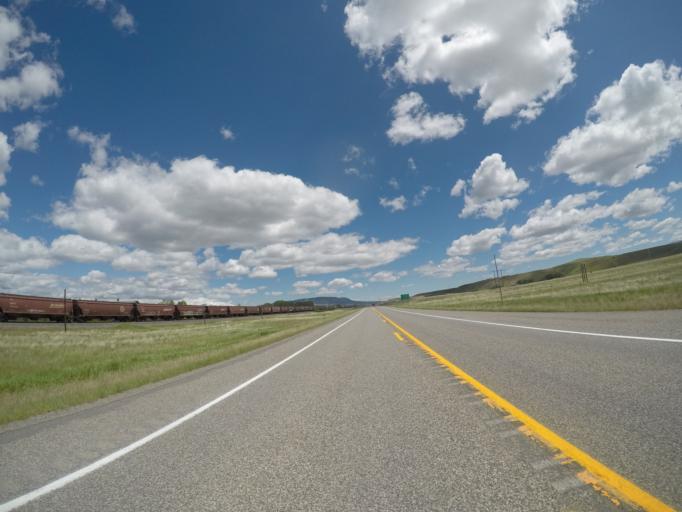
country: US
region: Montana
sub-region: Park County
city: Livingston
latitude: 45.6868
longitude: -110.5072
